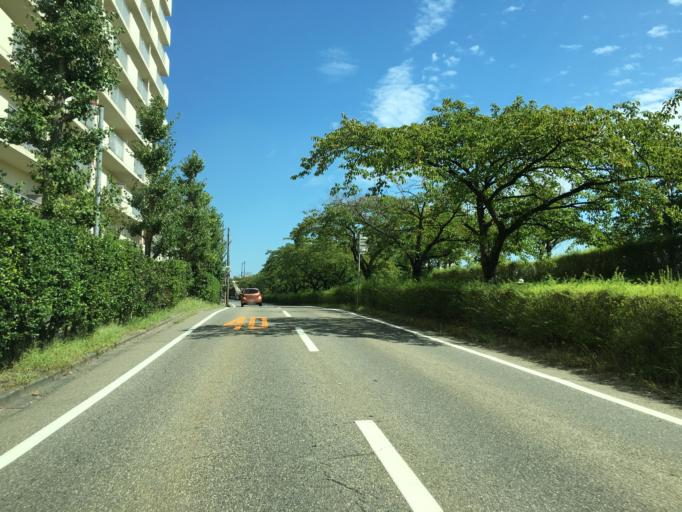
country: JP
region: Niigata
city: Niigata-shi
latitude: 37.9152
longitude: 139.0463
